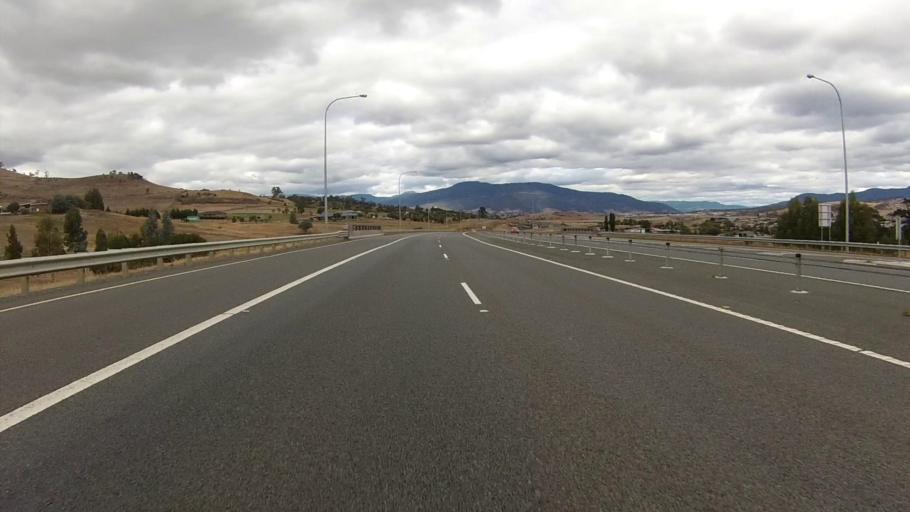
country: AU
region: Tasmania
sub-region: Brighton
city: Bridgewater
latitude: -42.6990
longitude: 147.2760
